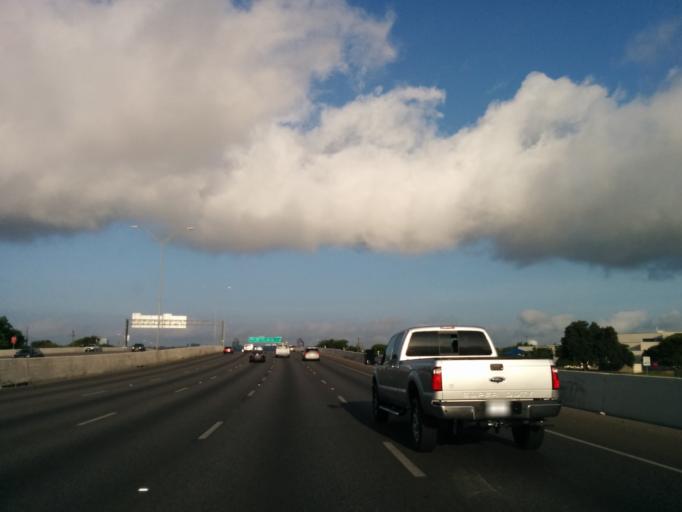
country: US
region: Texas
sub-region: Bexar County
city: Castle Hills
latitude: 29.5204
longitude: -98.5171
